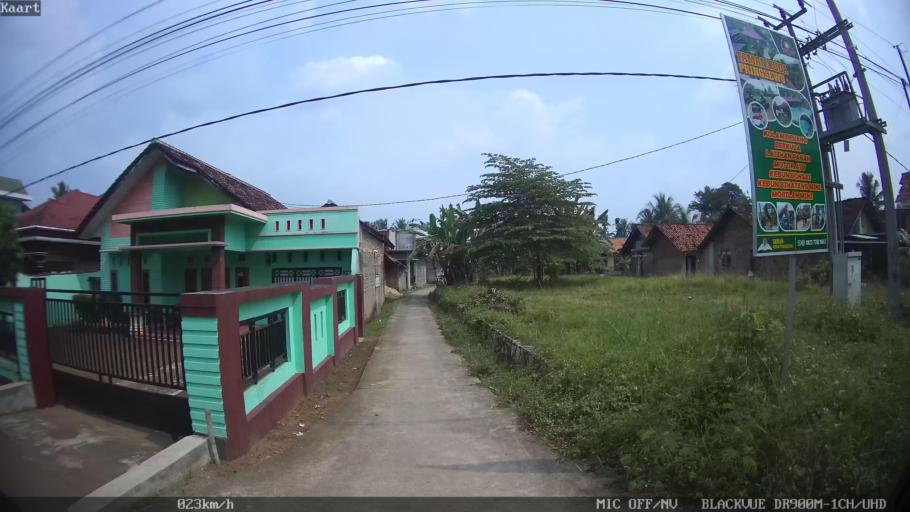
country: ID
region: Lampung
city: Gadingrejo
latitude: -5.3499
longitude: 105.0262
